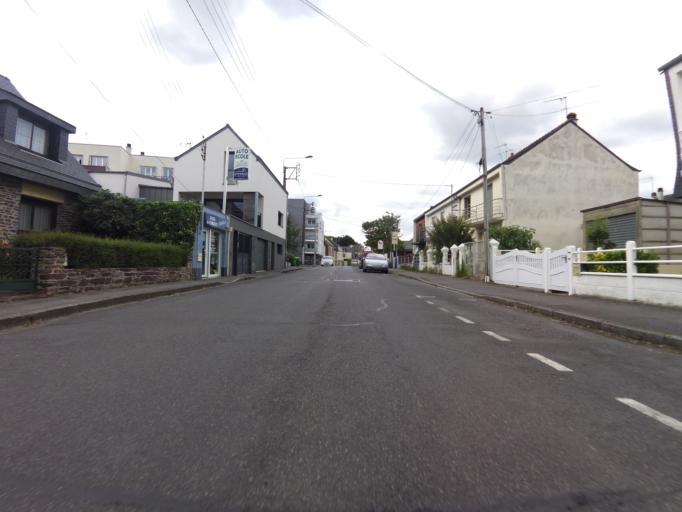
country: FR
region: Brittany
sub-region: Departement d'Ille-et-Vilaine
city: Rennes
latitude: 48.0900
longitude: -1.6722
